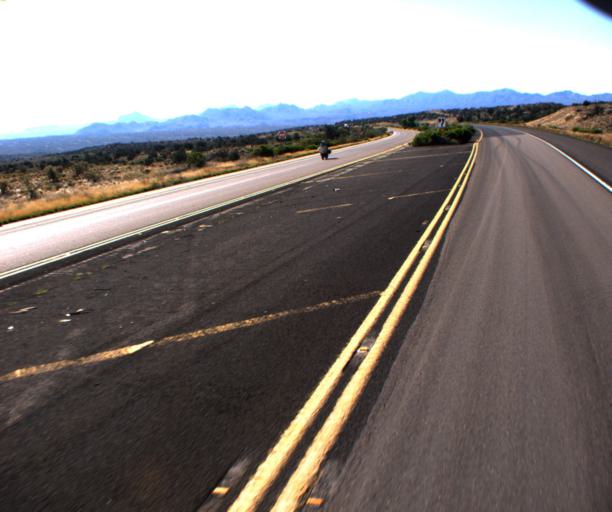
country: US
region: Arizona
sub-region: Mohave County
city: New Kingman-Butler
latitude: 35.1495
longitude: -113.6900
